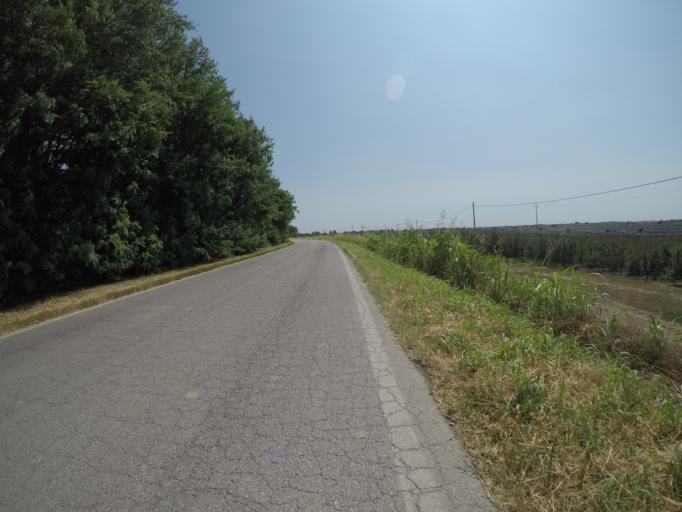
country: IT
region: Veneto
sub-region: Provincia di Rovigo
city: Pincara
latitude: 45.0014
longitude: 11.6415
